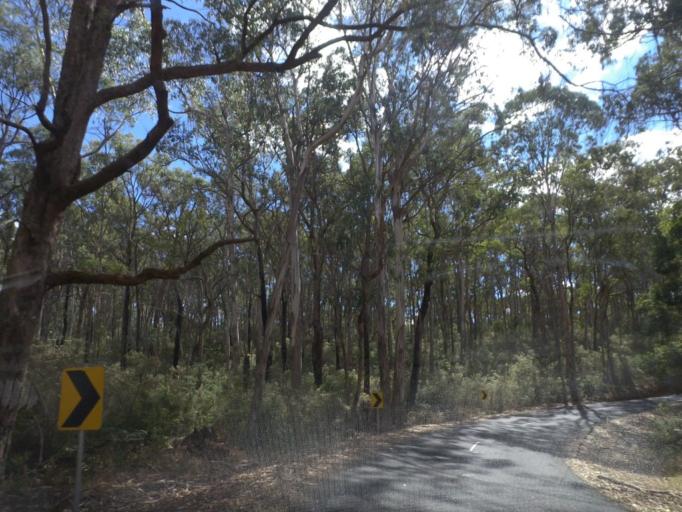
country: AU
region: Victoria
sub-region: Murrindindi
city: Alexandra
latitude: -37.3373
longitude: 145.9622
